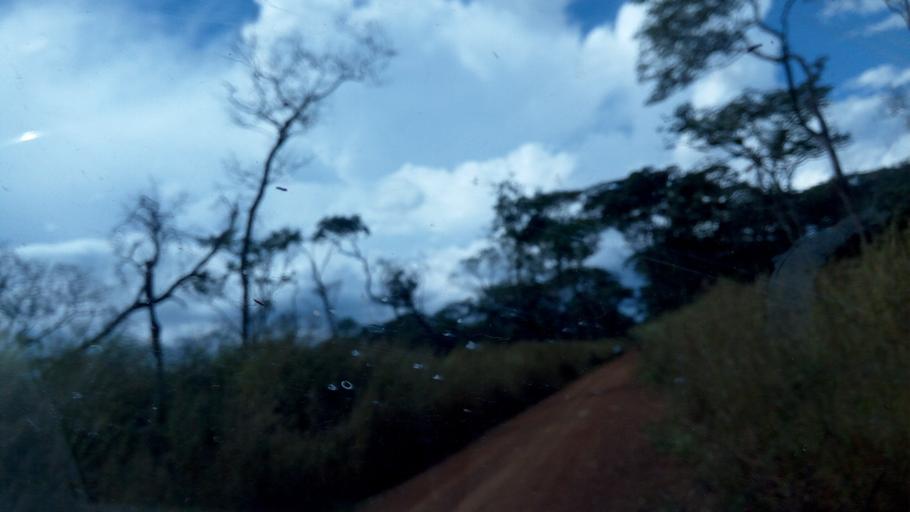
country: ZM
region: Northern
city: Kaputa
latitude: -8.1857
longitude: 29.0837
